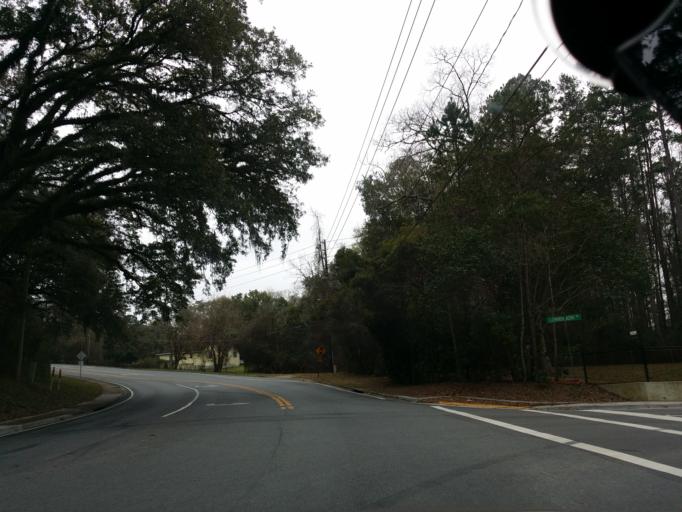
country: US
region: Florida
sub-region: Leon County
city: Tallahassee
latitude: 30.4869
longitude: -84.2299
